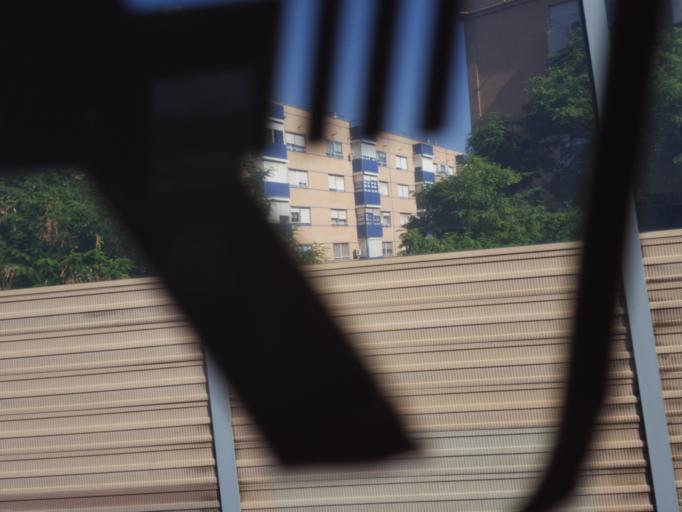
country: ES
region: Murcia
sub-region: Murcia
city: Murcia
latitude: 37.9835
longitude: -1.1404
